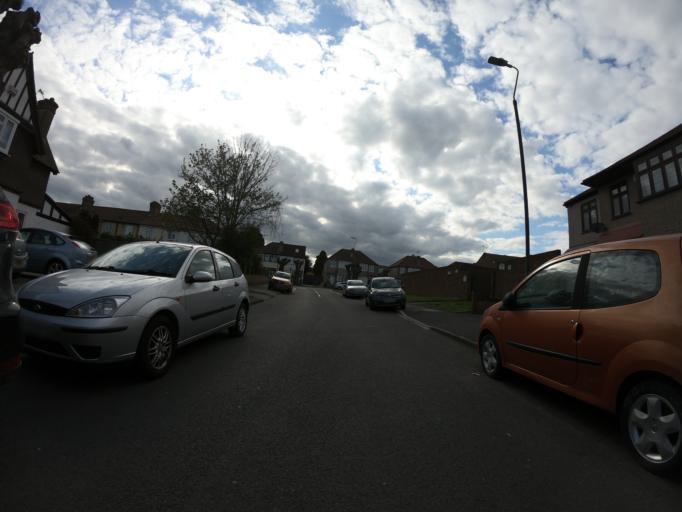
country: GB
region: England
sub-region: Greater London
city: Belvedere
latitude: 51.4797
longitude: 0.1406
